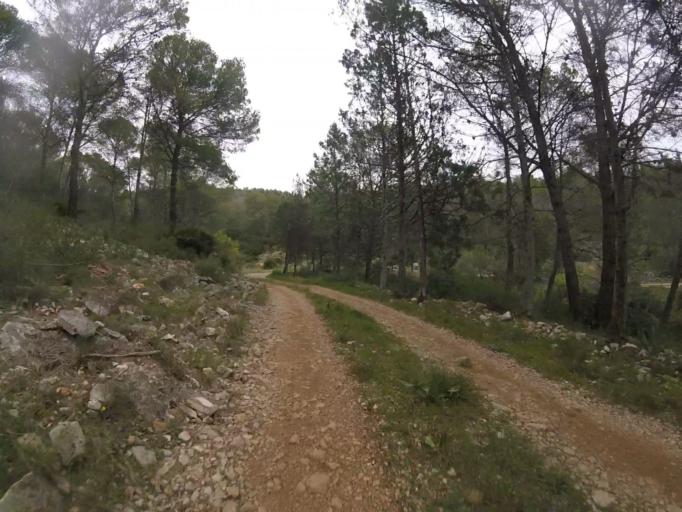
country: ES
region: Valencia
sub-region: Provincia de Castello
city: Santa Magdalena de Pulpis
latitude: 40.3205
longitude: 0.2824
